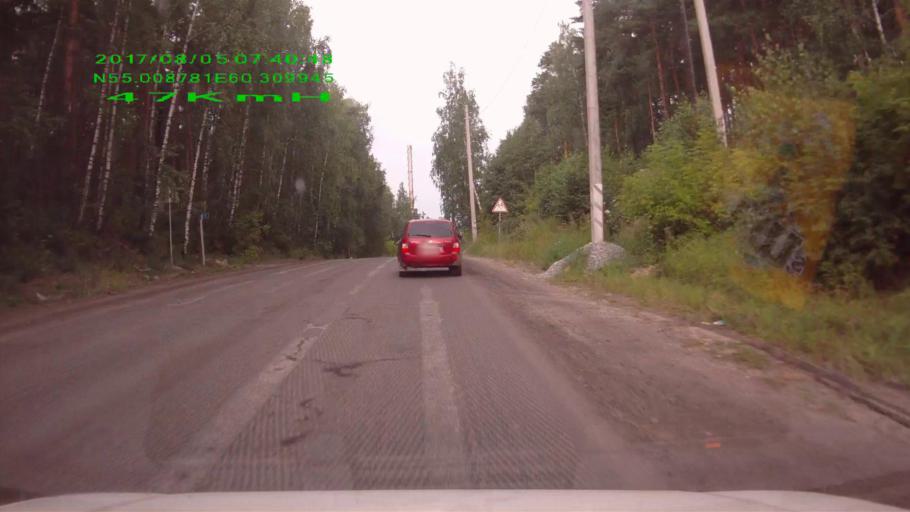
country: RU
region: Chelyabinsk
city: Chebarkul'
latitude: 55.0089
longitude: 60.3096
